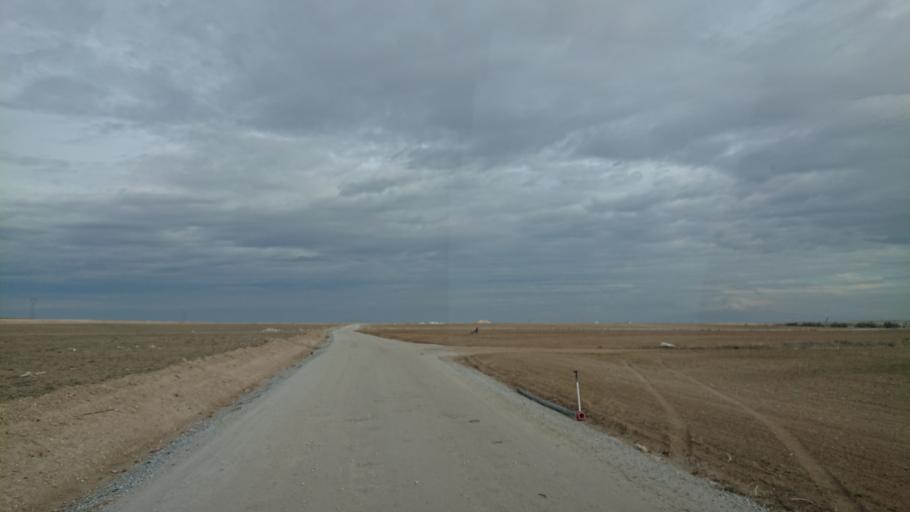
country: TR
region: Aksaray
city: Sultanhani
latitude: 38.1347
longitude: 33.5529
